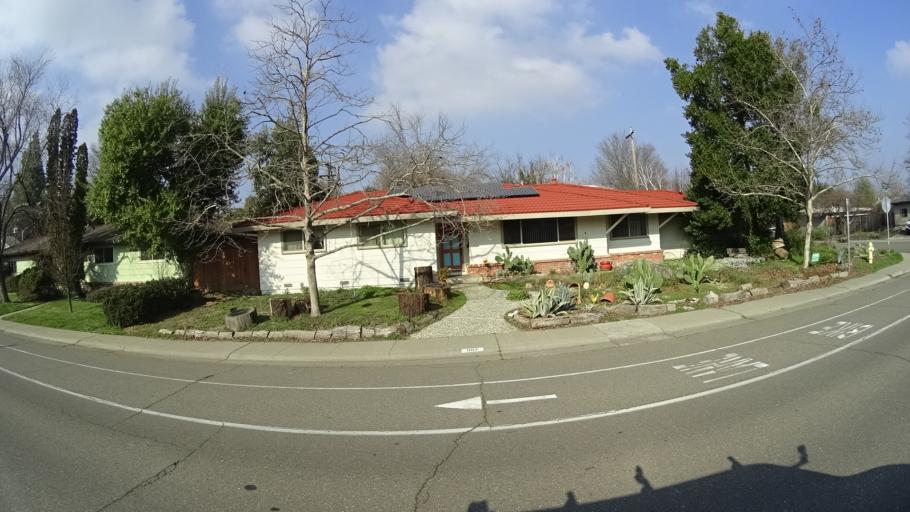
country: US
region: California
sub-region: Yolo County
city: Davis
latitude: 38.5562
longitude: -121.7609
